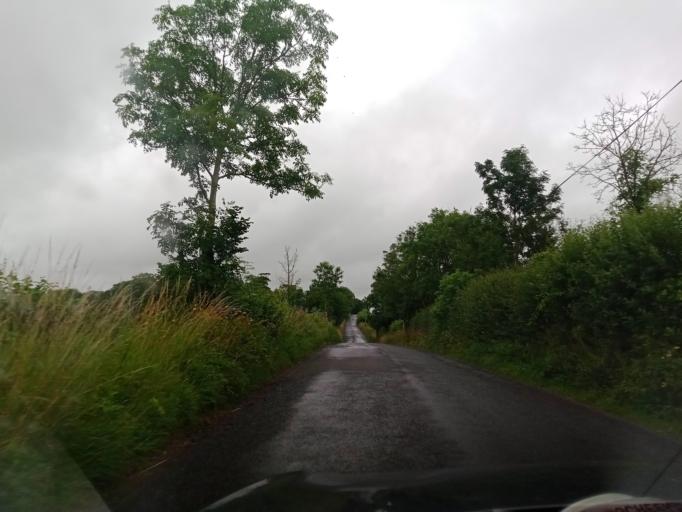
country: IE
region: Leinster
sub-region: Laois
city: Abbeyleix
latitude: 52.9148
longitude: -7.2909
